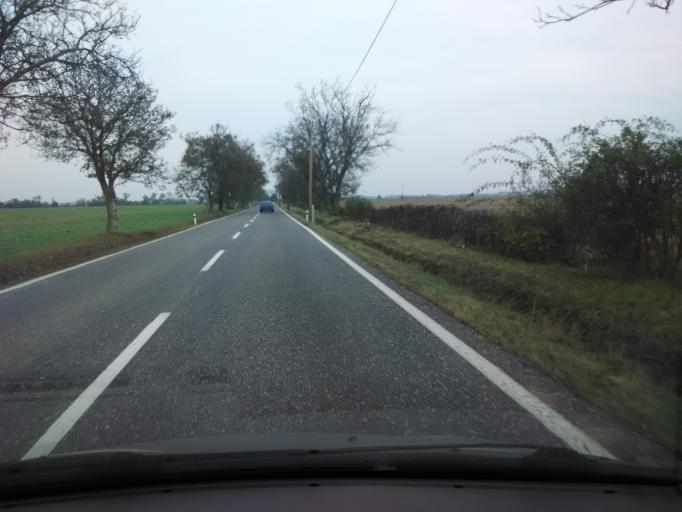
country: SK
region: Nitriansky
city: Zeliezovce
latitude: 48.0602
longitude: 18.5053
